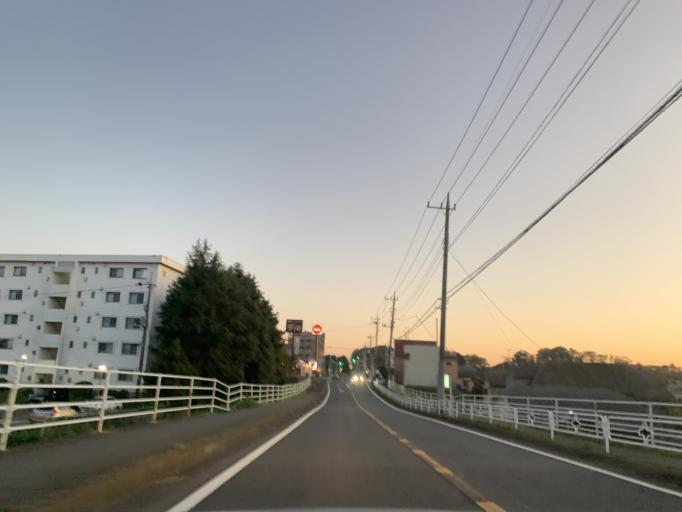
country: JP
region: Chiba
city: Nagareyama
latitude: 35.8931
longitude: 139.9006
